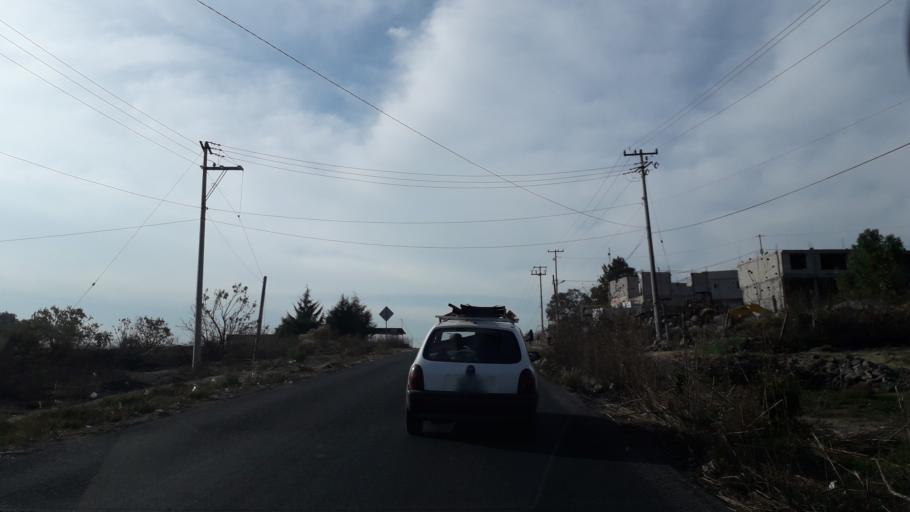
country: MX
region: Puebla
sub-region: Puebla
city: San Andres Azumiatla
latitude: 18.9122
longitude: -98.2422
